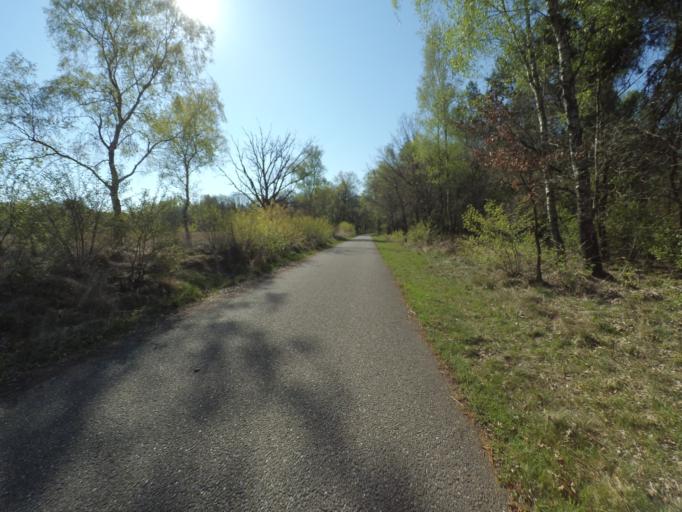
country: NL
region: Gelderland
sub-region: Gemeente Ede
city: Harskamp
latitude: 52.1844
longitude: 5.8126
